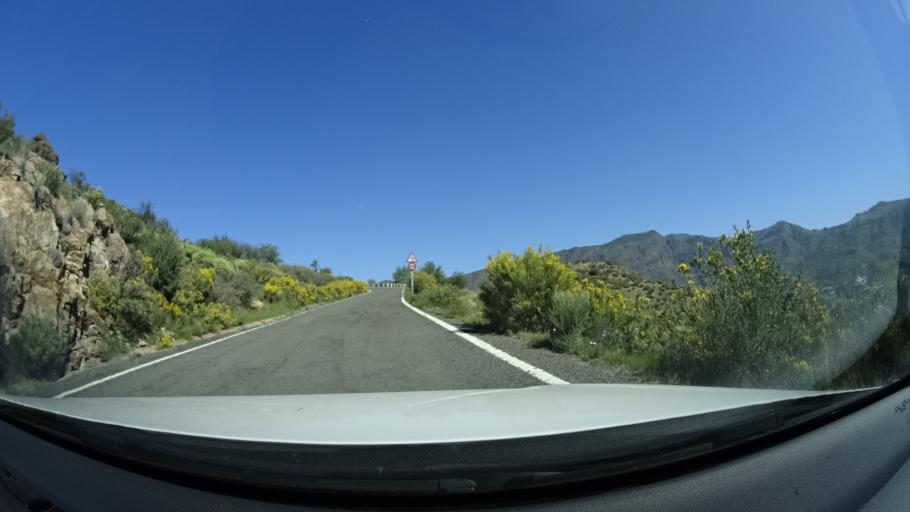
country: ES
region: Canary Islands
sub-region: Provincia de Las Palmas
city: Tejeda
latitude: 27.9893
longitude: -15.6376
